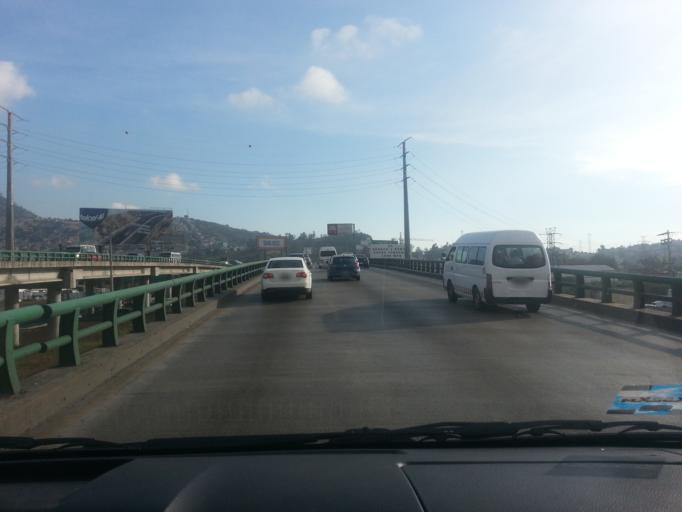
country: MX
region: Mexico City
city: Gustavo A. Madero
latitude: 19.5140
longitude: -99.1016
